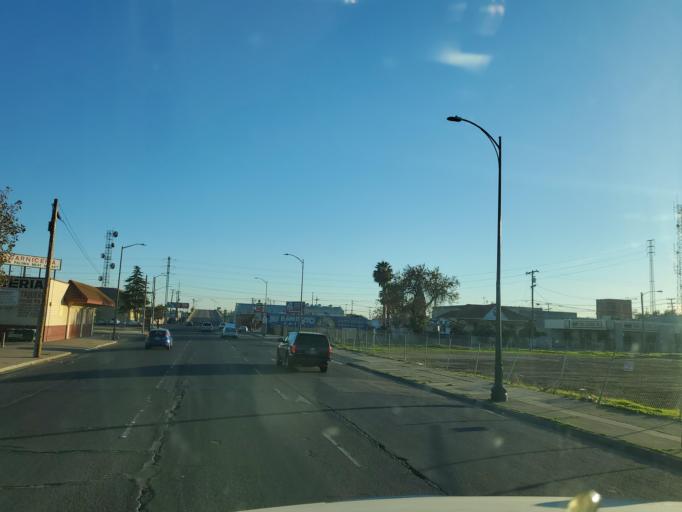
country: US
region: California
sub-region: San Joaquin County
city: Stockton
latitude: 37.9492
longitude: -121.2902
